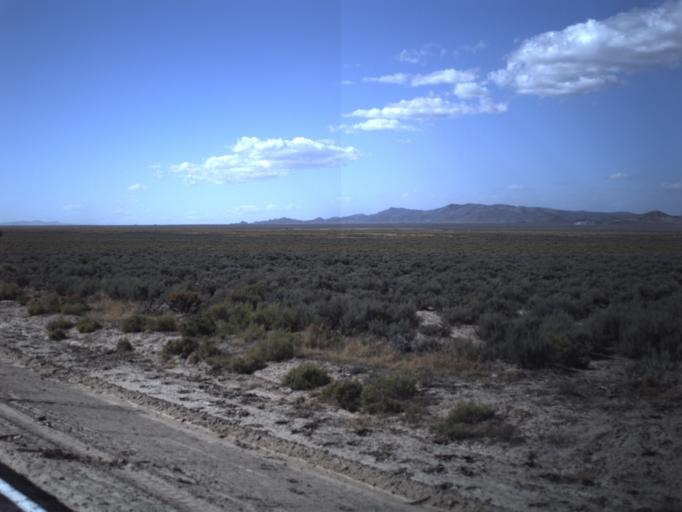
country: US
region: Utah
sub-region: Beaver County
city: Milford
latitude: 38.4848
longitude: -112.9911
